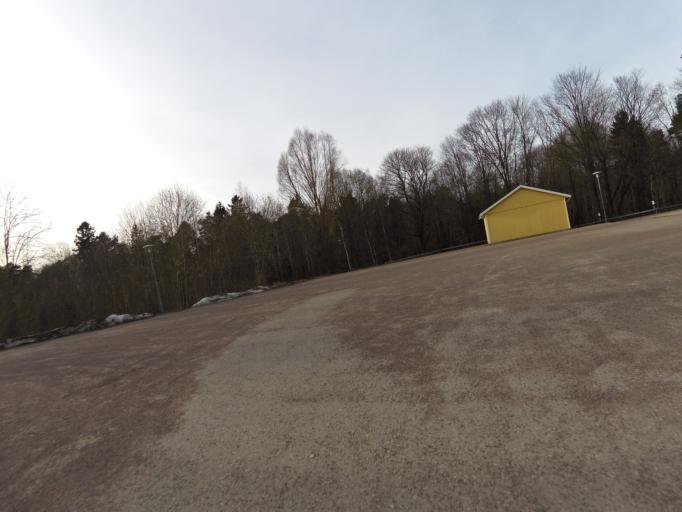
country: SE
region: Gaevleborg
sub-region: Gavle Kommun
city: Gavle
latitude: 60.6754
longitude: 17.1097
